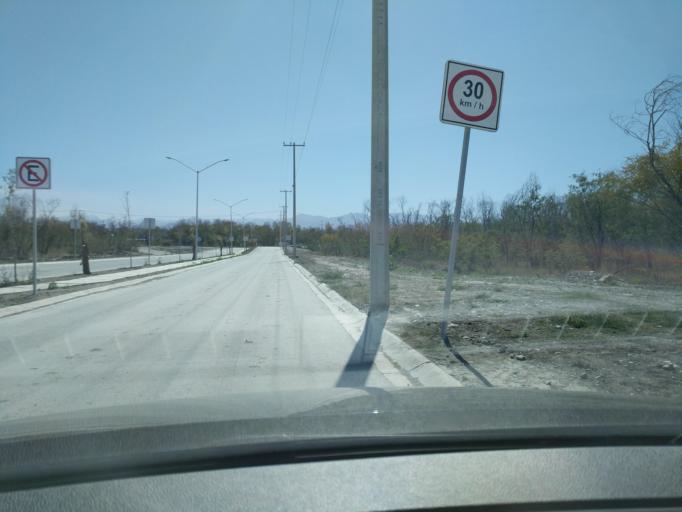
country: MX
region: Nuevo Leon
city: Juarez
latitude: 25.6382
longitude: -100.0830
